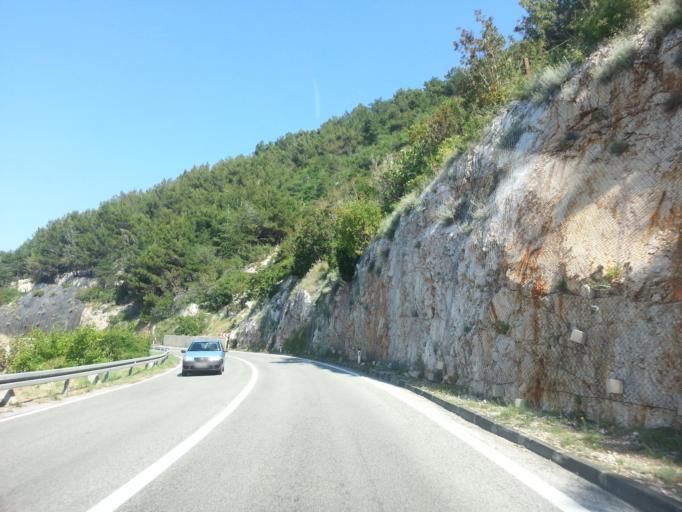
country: HR
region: Primorsko-Goranska
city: Kraljevica
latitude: 45.2927
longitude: 14.5701
